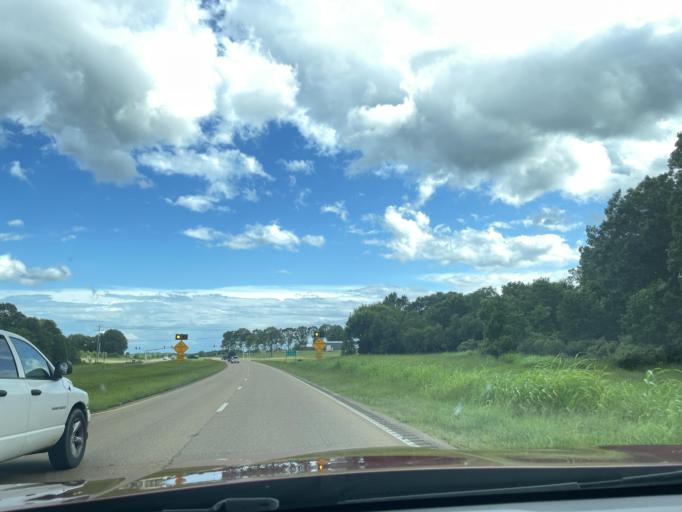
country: US
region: Mississippi
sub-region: Madison County
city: Flora
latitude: 32.5411
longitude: -90.3209
